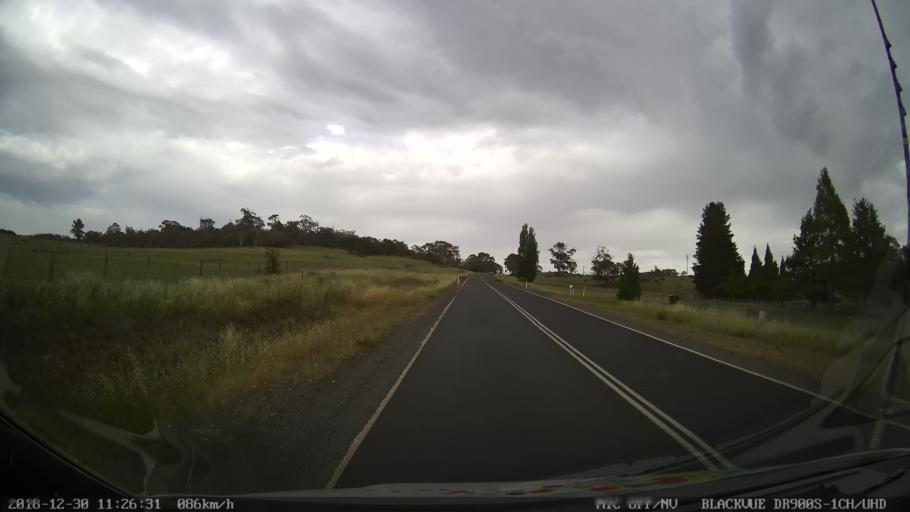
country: AU
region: New South Wales
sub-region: Snowy River
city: Jindabyne
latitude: -36.4678
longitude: 148.6331
